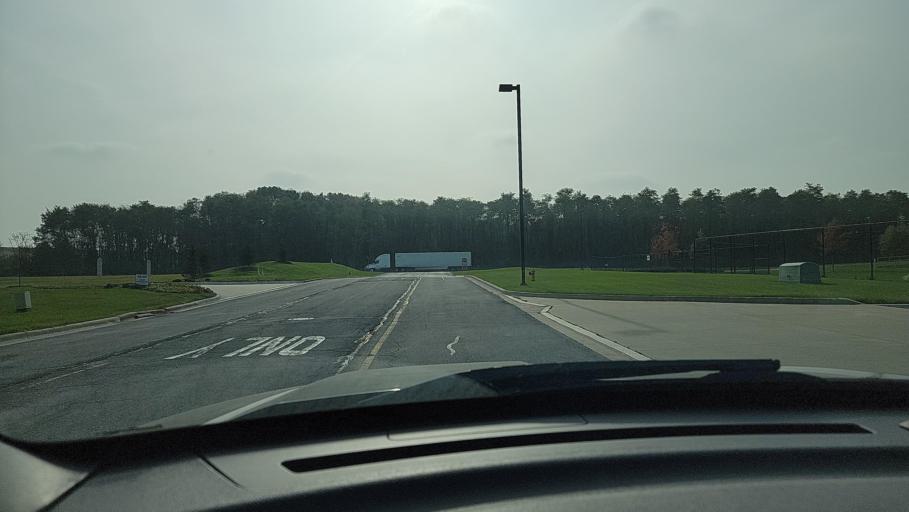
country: US
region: Indiana
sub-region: Porter County
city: Burns Harbor
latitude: 41.6068
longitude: -87.1560
